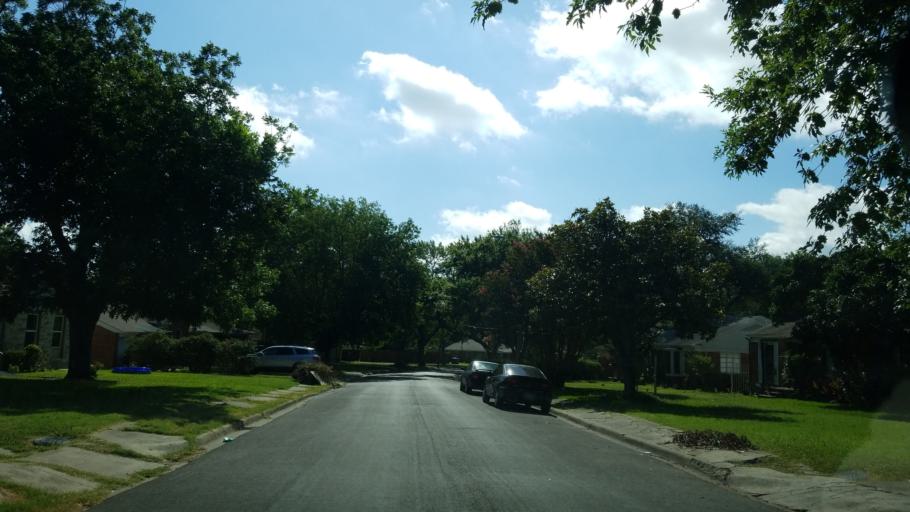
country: US
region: Texas
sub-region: Dallas County
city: Dallas
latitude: 32.7153
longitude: -96.8012
